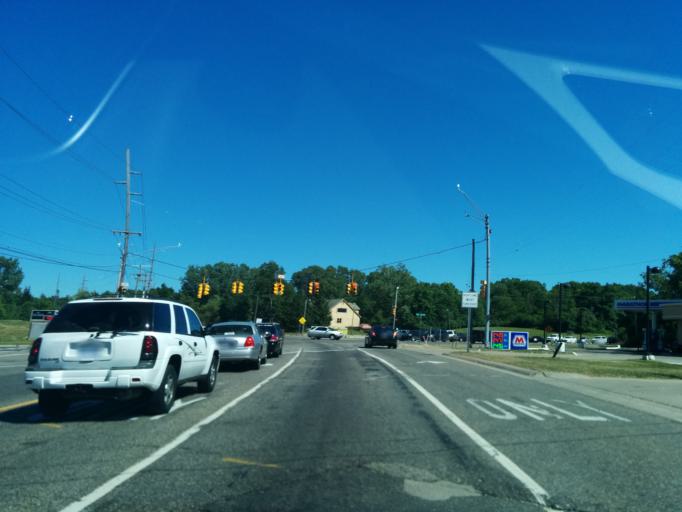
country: US
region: Michigan
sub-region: Oakland County
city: Wolverine Lake
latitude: 42.5413
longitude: -83.4385
